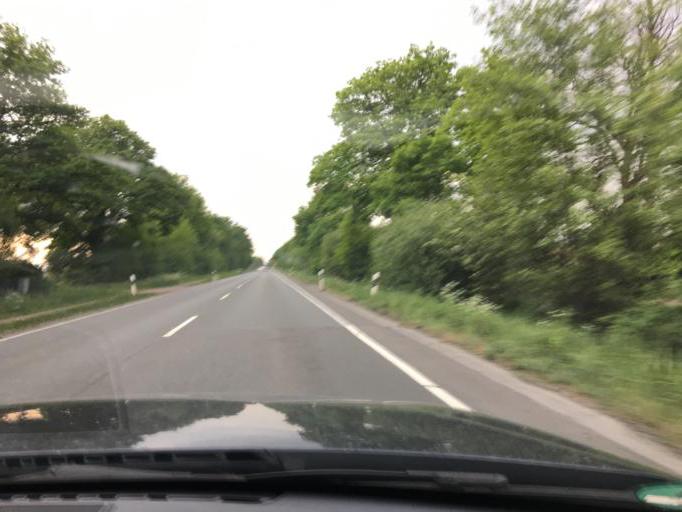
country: DE
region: North Rhine-Westphalia
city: Emsdetten
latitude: 52.1402
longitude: 7.5675
